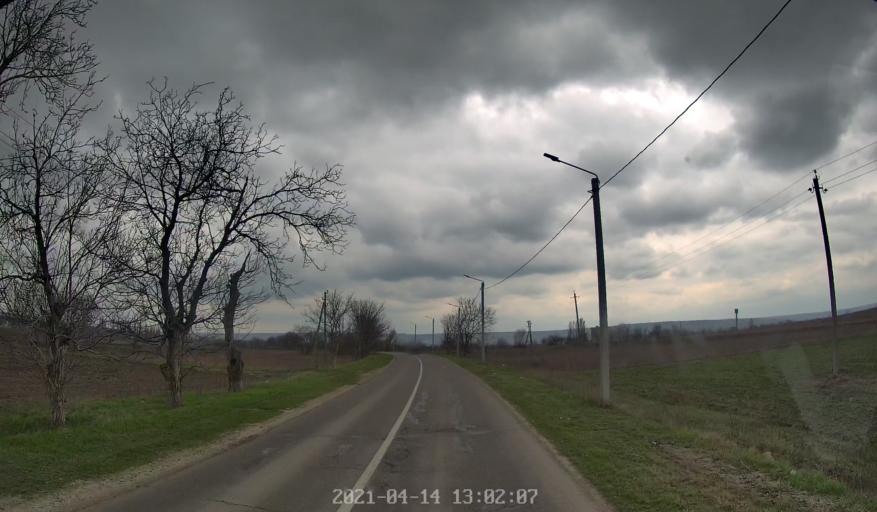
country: MD
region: Chisinau
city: Vadul lui Voda
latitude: 47.1261
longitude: 29.1119
